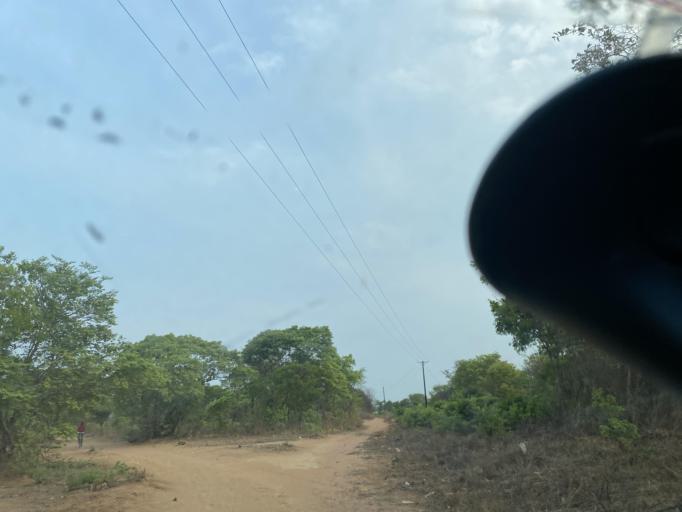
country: ZM
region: Lusaka
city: Chongwe
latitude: -15.2058
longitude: 28.4990
